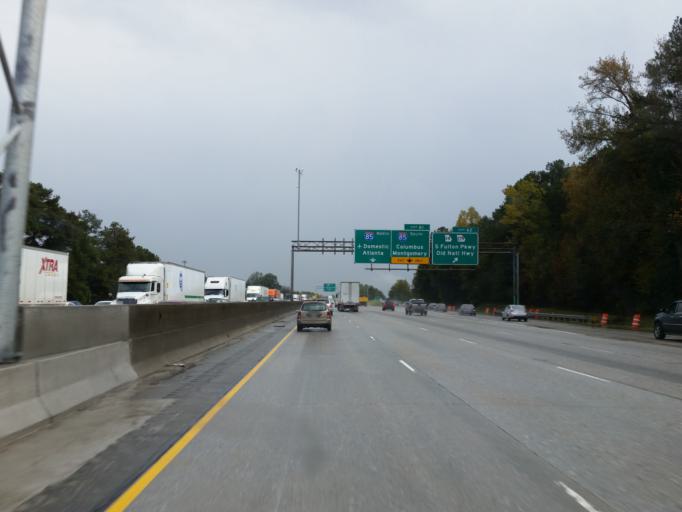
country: US
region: Georgia
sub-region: Fulton County
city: College Park
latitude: 33.6276
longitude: -84.4889
